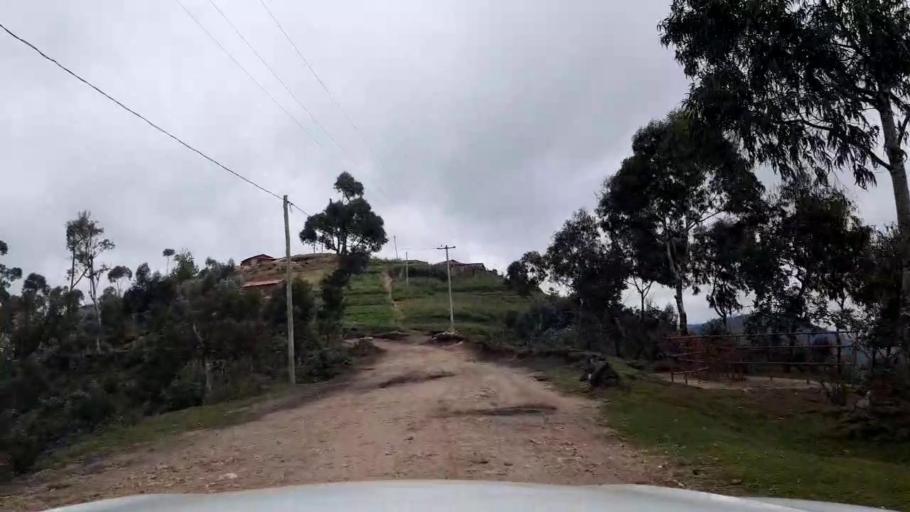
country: RW
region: Western Province
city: Kibuye
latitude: -1.9385
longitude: 29.4640
